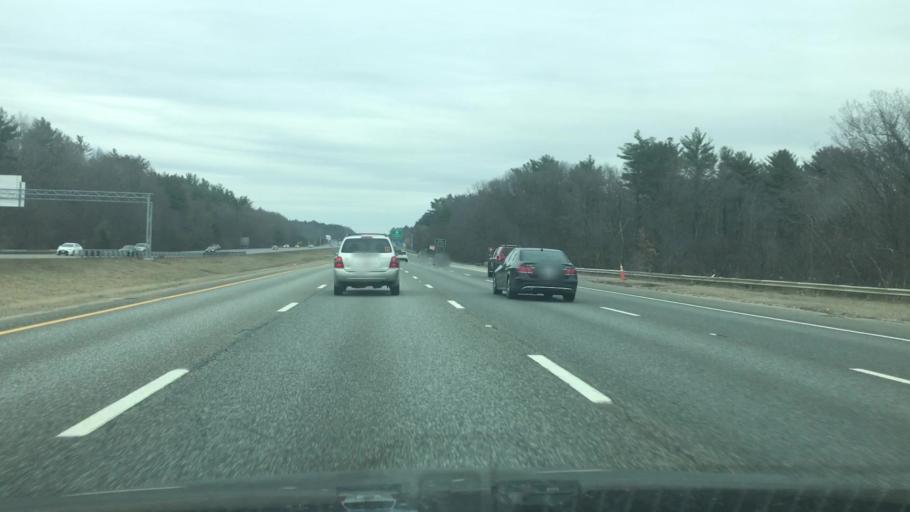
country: US
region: Massachusetts
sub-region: Essex County
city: Boxford
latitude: 42.6860
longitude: -70.9736
